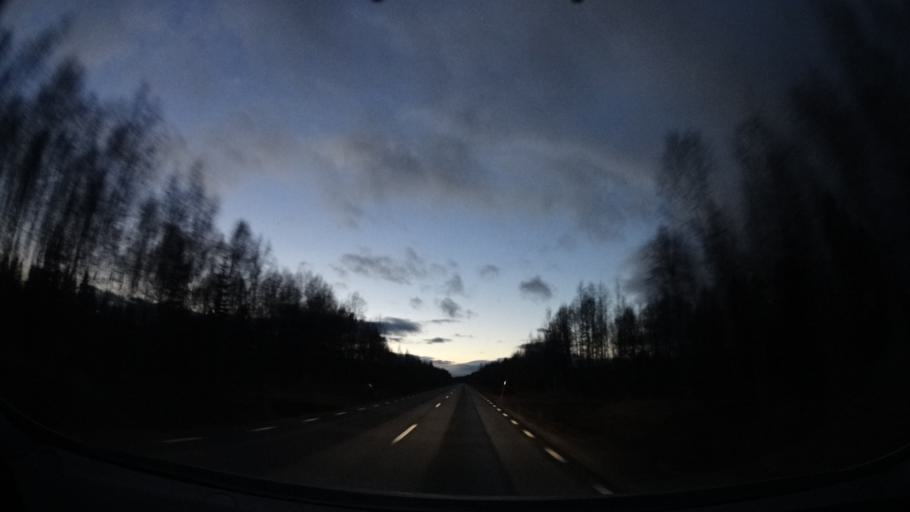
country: SE
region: Vaesterbotten
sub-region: Dorotea Kommun
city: Dorotea
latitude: 64.2490
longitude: 16.6126
